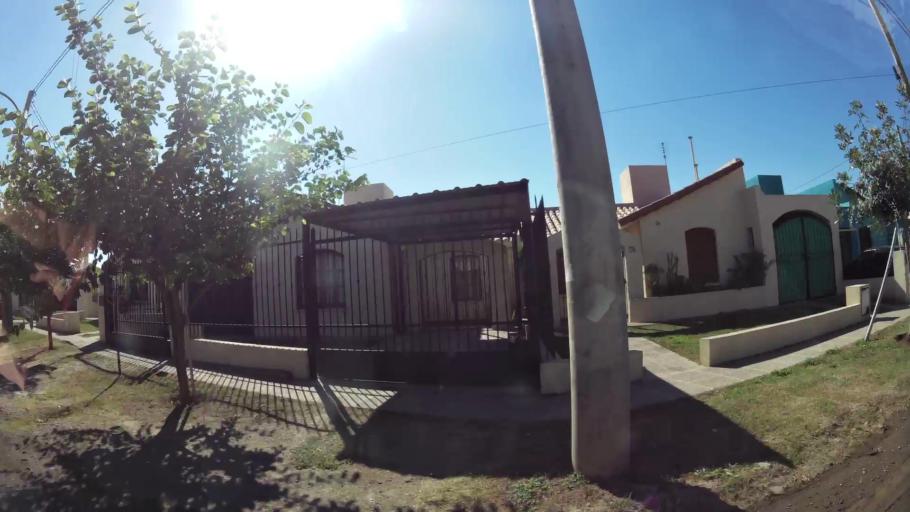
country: AR
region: Cordoba
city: Villa Allende
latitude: -31.3386
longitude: -64.2402
